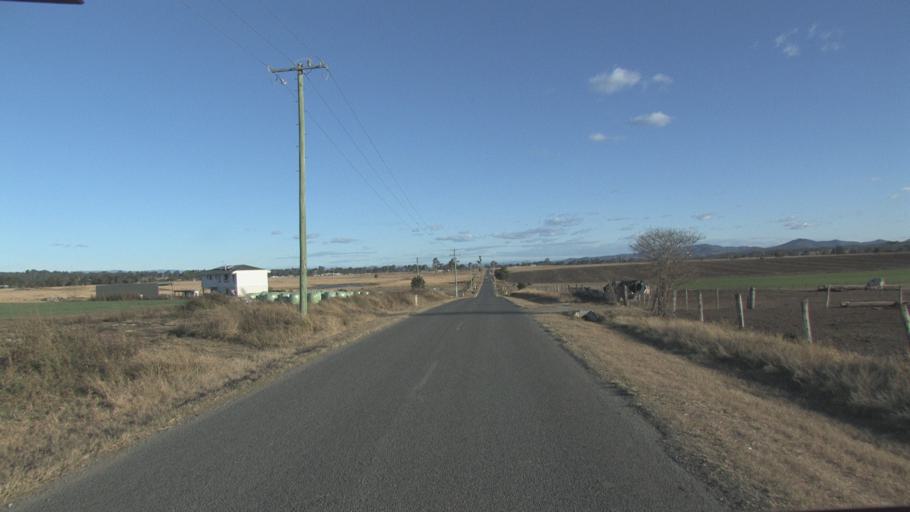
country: AU
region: Queensland
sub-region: Logan
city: Cedar Vale
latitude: -27.8587
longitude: 152.9594
